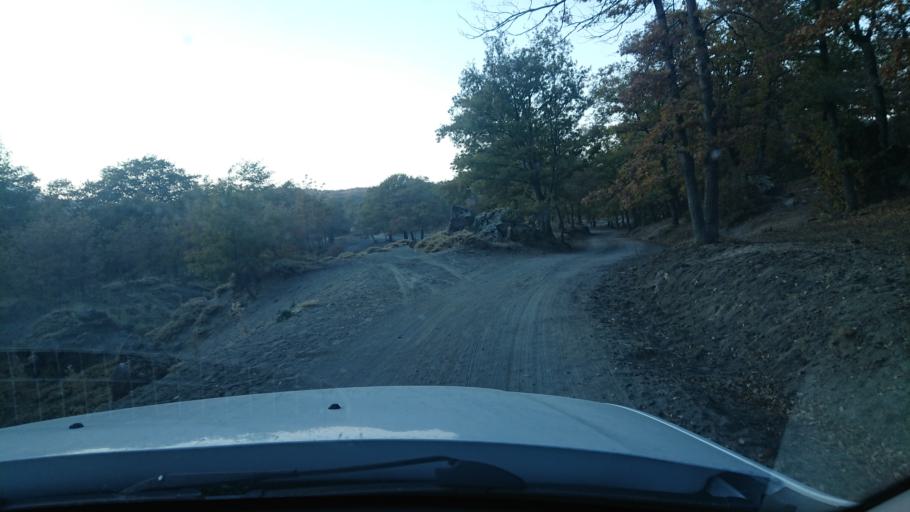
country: TR
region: Aksaray
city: Taspinar
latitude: 38.1654
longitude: 34.2070
